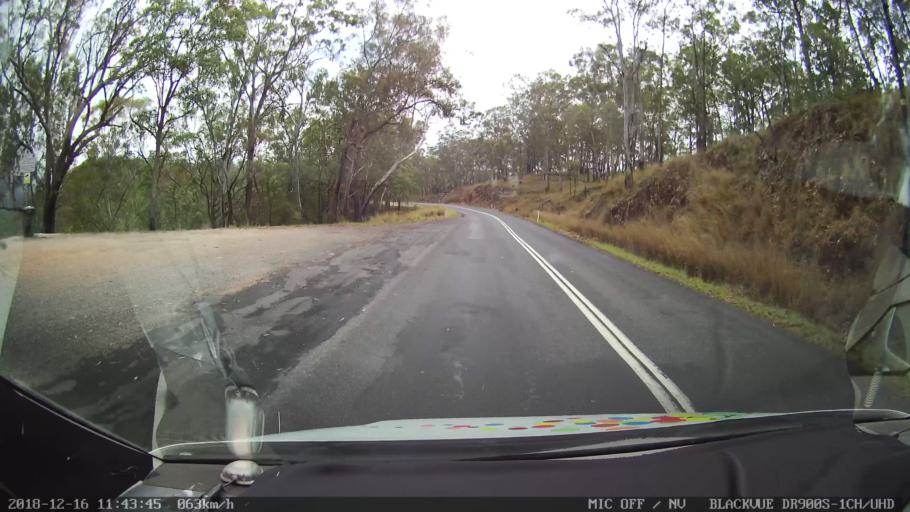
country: AU
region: New South Wales
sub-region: Tenterfield Municipality
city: Carrolls Creek
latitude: -28.9436
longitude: 152.2191
